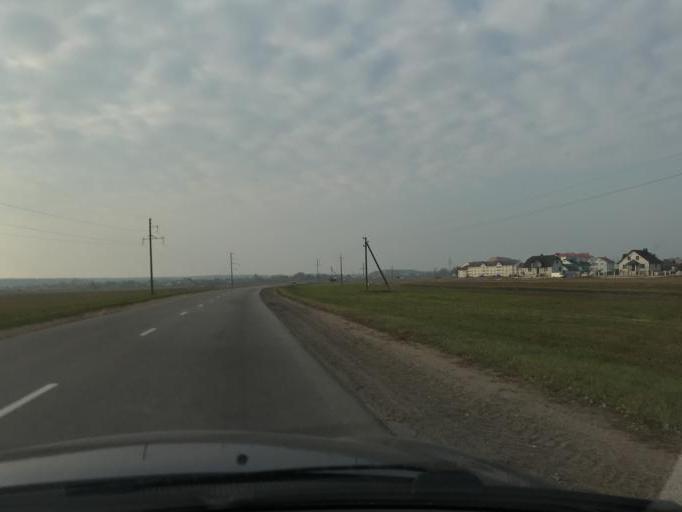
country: BY
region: Grodnenskaya
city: Lida
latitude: 53.8587
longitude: 25.2946
